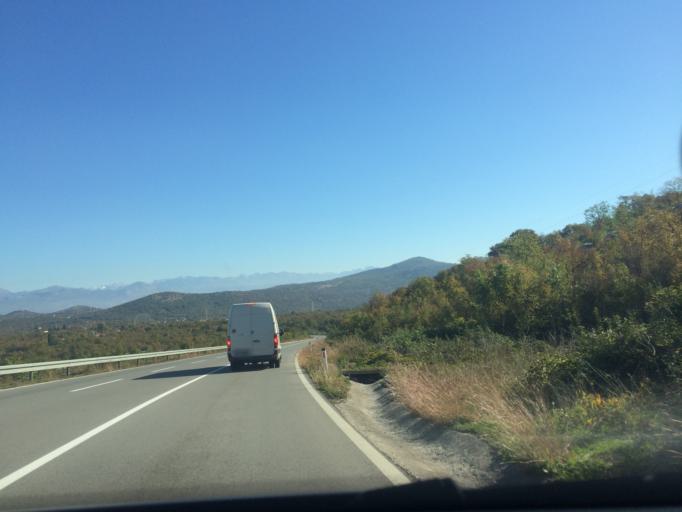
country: ME
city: Mojanovici
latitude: 42.3901
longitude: 19.1172
